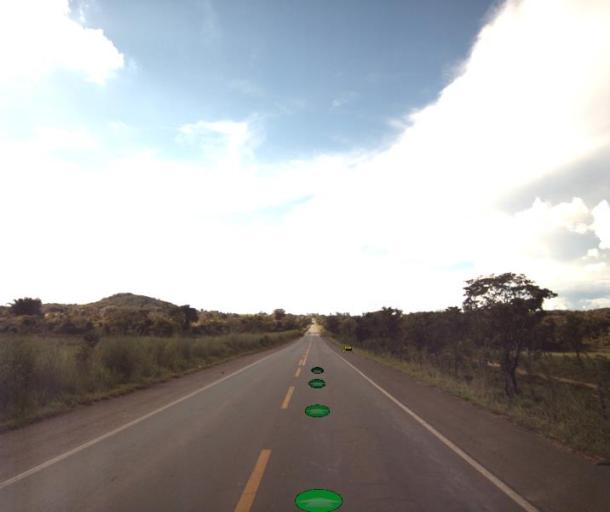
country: BR
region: Goias
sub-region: Rialma
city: Rialma
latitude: -15.4395
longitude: -49.5089
